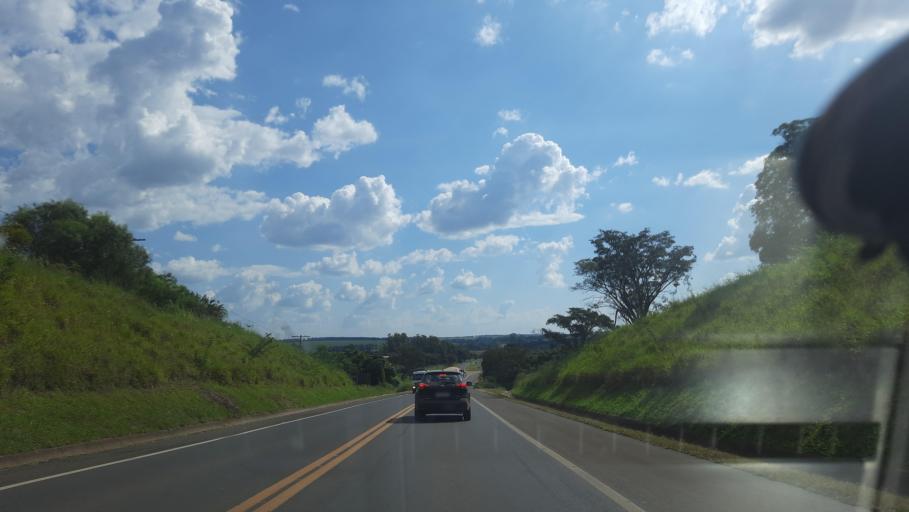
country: BR
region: Sao Paulo
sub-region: Casa Branca
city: Casa Branca
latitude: -21.7390
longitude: -46.9758
